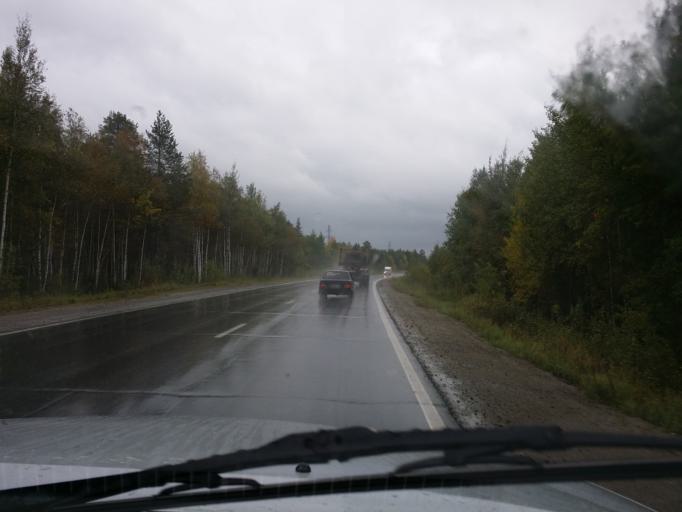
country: RU
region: Khanty-Mansiyskiy Avtonomnyy Okrug
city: Megion
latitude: 61.1442
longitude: 75.7566
